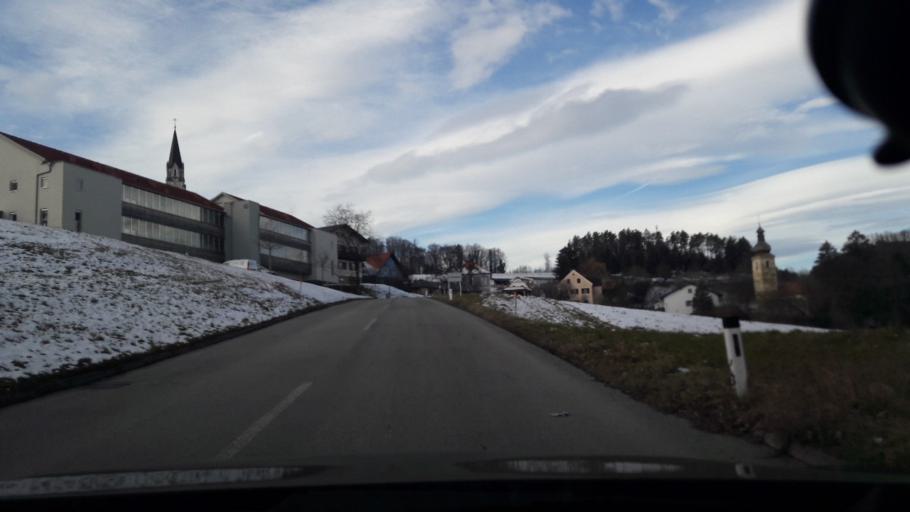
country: AT
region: Styria
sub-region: Politischer Bezirk Graz-Umgebung
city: Sankt Bartholoma
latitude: 47.0705
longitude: 15.2601
